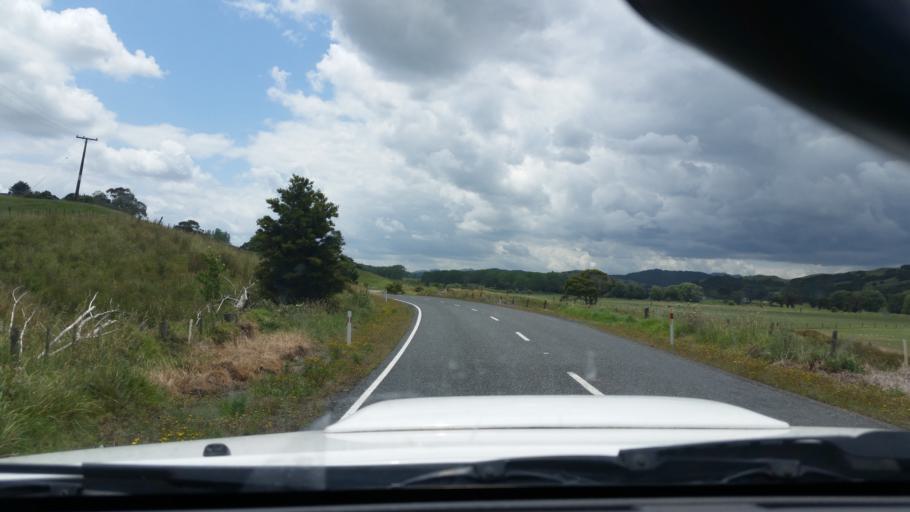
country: NZ
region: Northland
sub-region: Kaipara District
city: Dargaville
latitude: -35.8623
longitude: 173.8439
